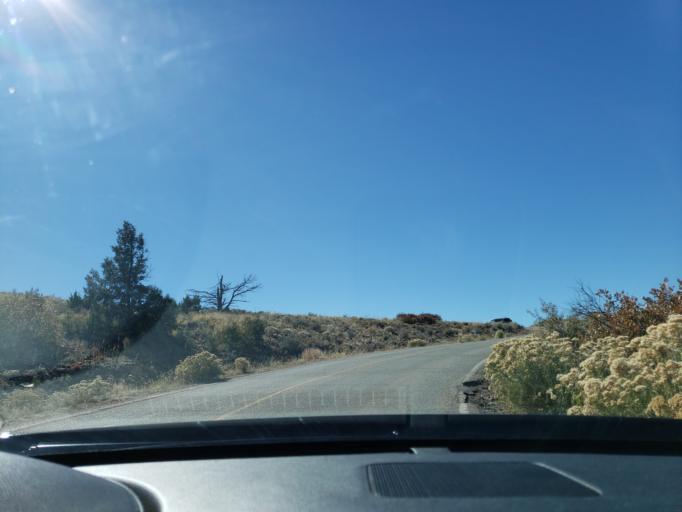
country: US
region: Colorado
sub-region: Fremont County
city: Canon City
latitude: 38.4708
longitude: -105.3092
